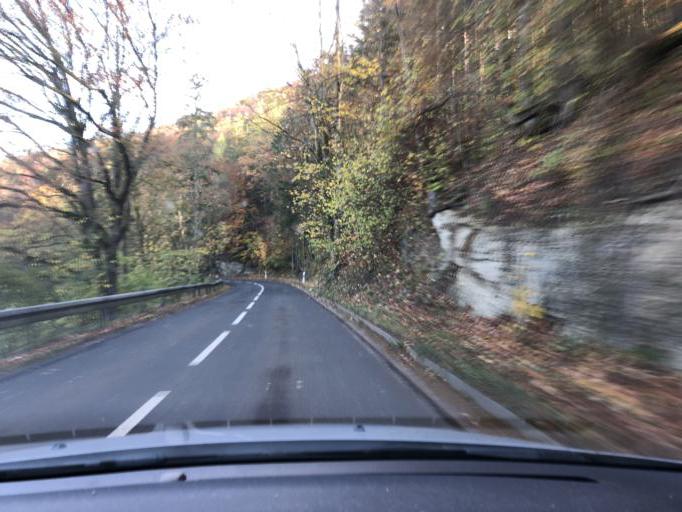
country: DE
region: Thuringia
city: Reurieth
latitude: 50.4411
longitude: 10.6474
